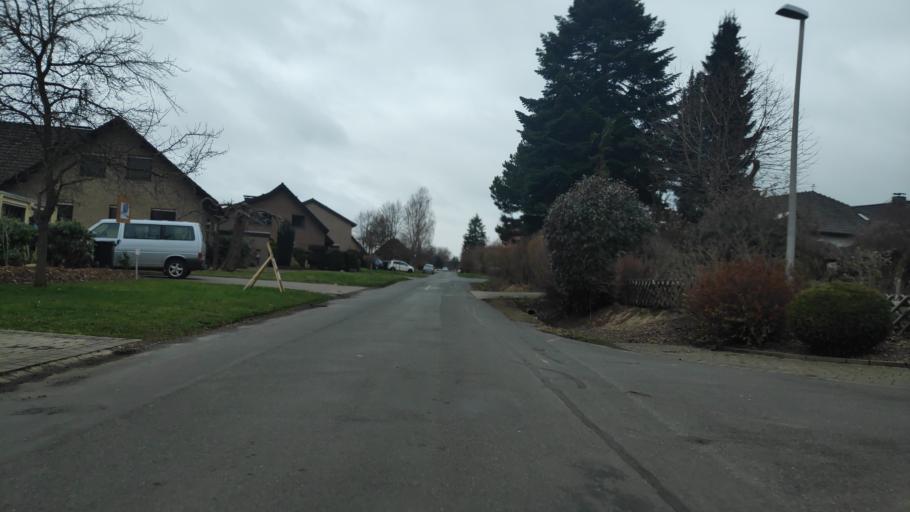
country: DE
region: North Rhine-Westphalia
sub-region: Regierungsbezirk Detmold
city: Minden
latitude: 52.2919
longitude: 8.8762
